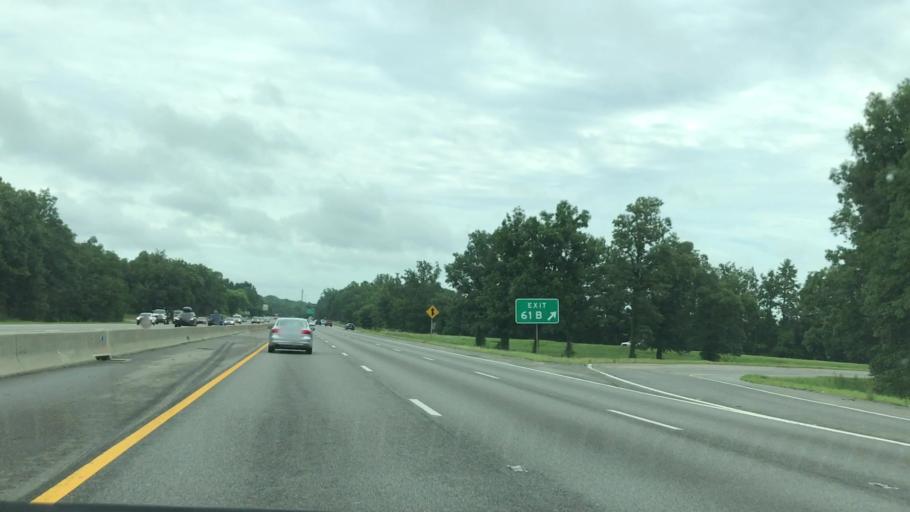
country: US
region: Virginia
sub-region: Chesterfield County
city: Chester
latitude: 37.3555
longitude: -77.4045
